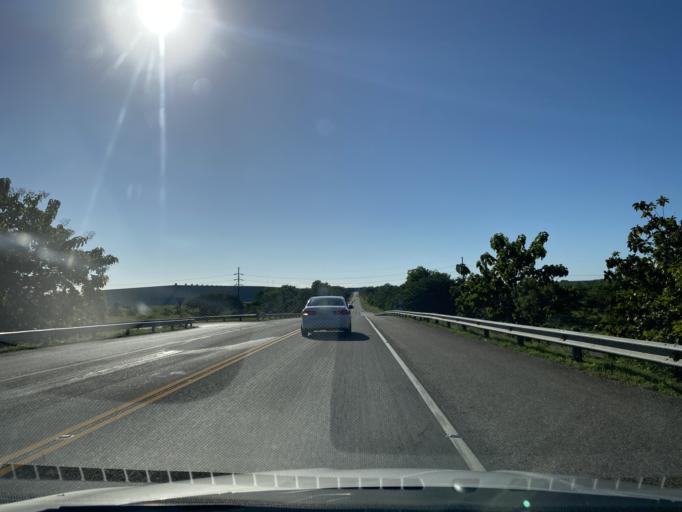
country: DO
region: Santo Domingo
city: Guerra
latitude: 18.5262
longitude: -69.7494
